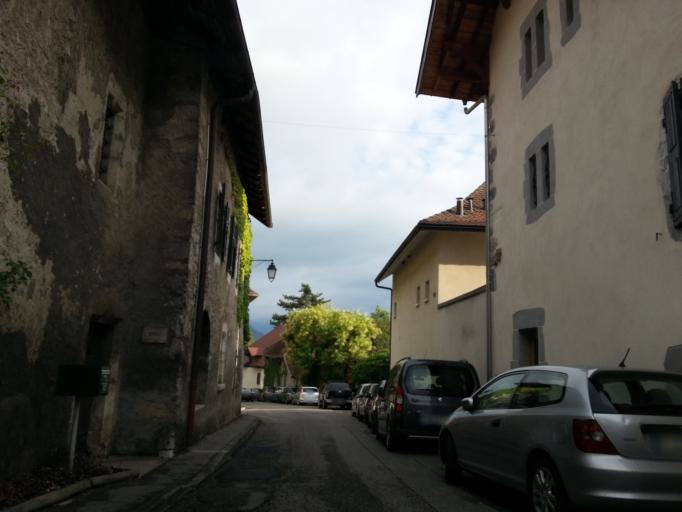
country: FR
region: Rhone-Alpes
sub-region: Departement de la Haute-Savoie
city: Talloires
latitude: 45.8385
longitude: 6.2152
